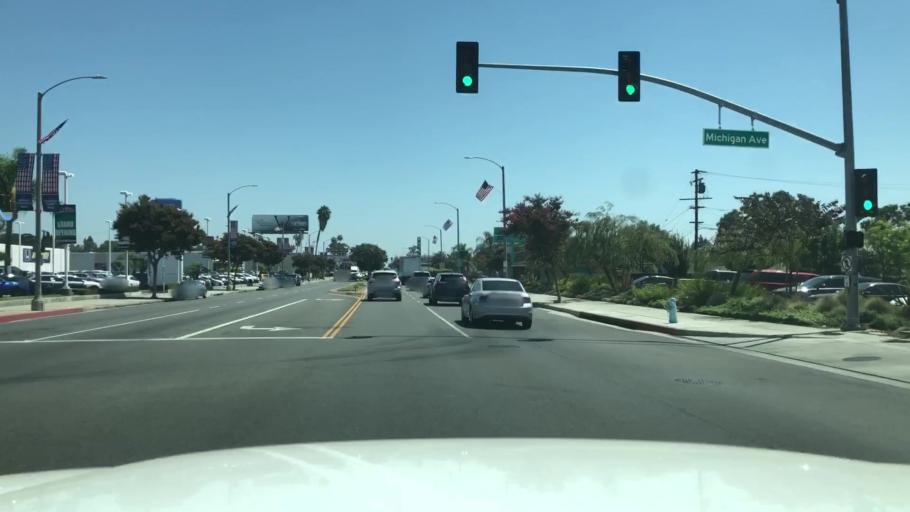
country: US
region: California
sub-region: Los Angeles County
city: South Whittier
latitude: 33.9597
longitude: -118.0269
